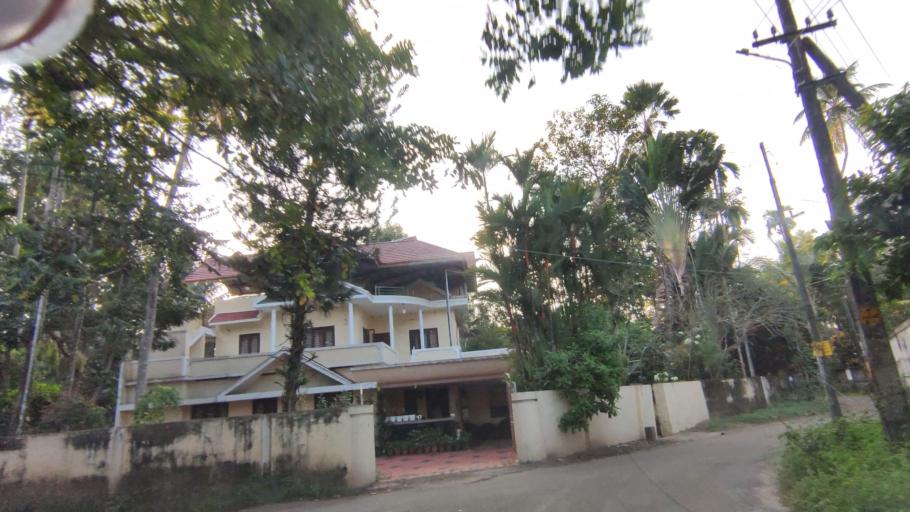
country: IN
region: Kerala
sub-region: Alappuzha
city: Shertallai
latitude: 9.6511
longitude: 76.3531
